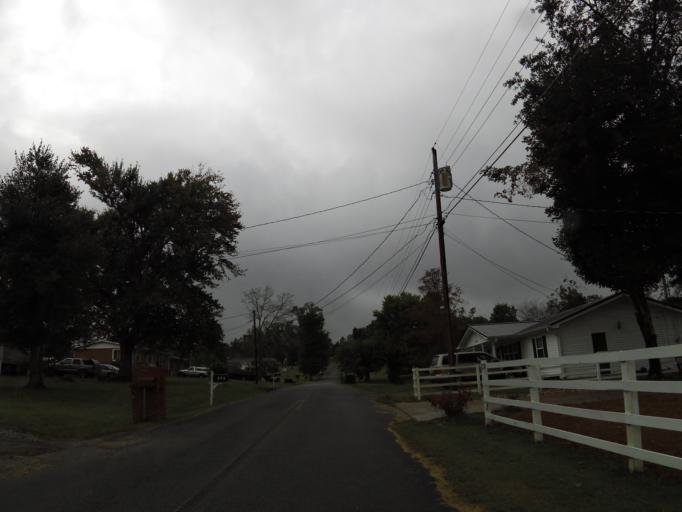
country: US
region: Tennessee
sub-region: Bradley County
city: Hopewell
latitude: 35.1888
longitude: -84.9432
